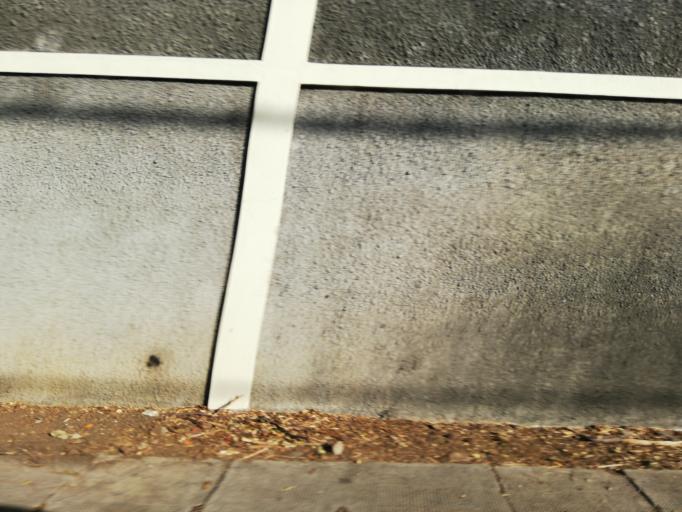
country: MU
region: Port Louis
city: Port Louis
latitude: -20.1709
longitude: 57.4812
